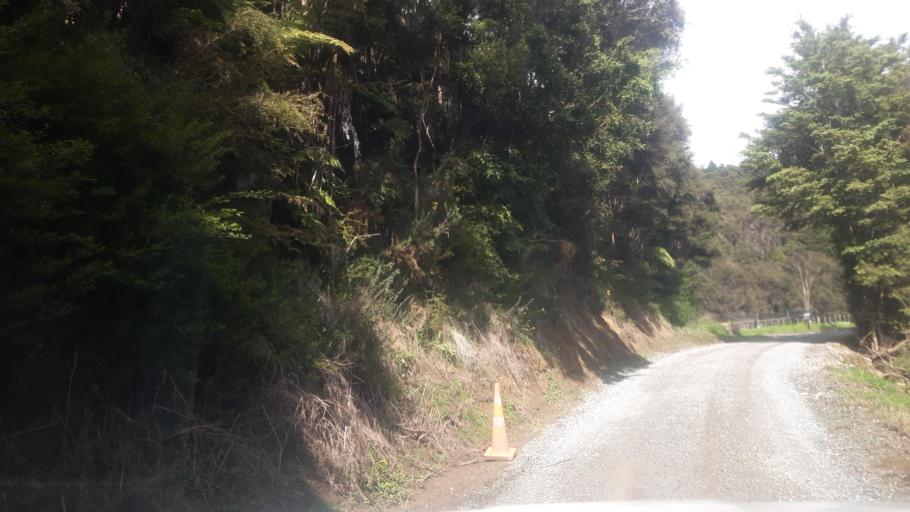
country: NZ
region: Northland
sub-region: Far North District
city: Taipa
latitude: -35.1174
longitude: 173.4335
